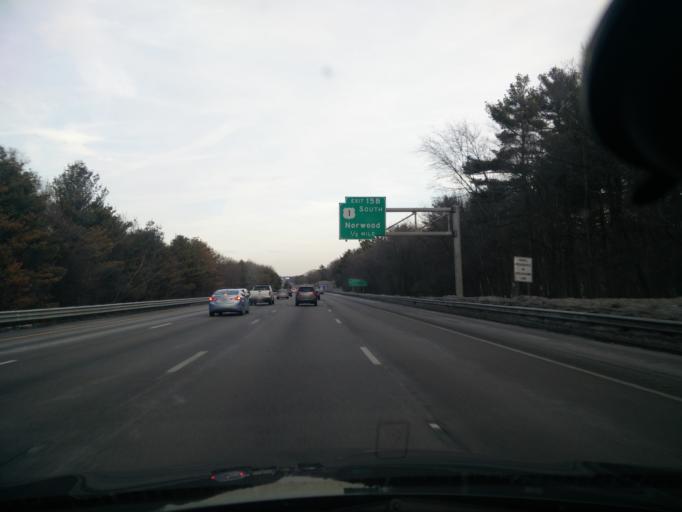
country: US
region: Massachusetts
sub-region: Norfolk County
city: Dedham
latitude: 42.2354
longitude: -71.1950
